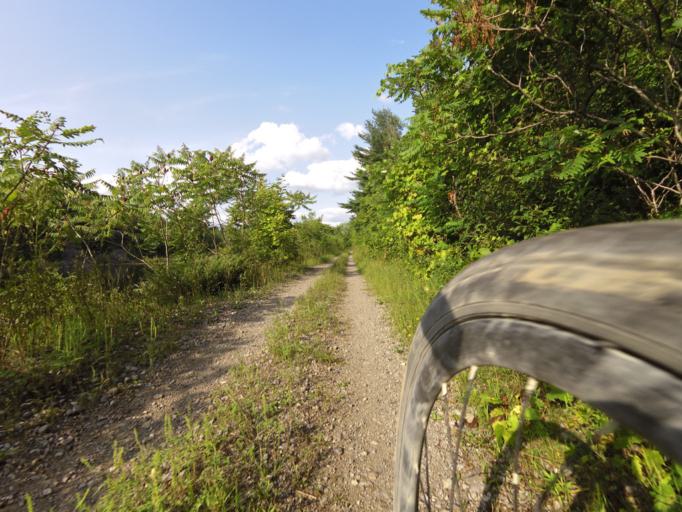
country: CA
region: Ontario
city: Kingston
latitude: 44.4379
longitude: -76.5338
